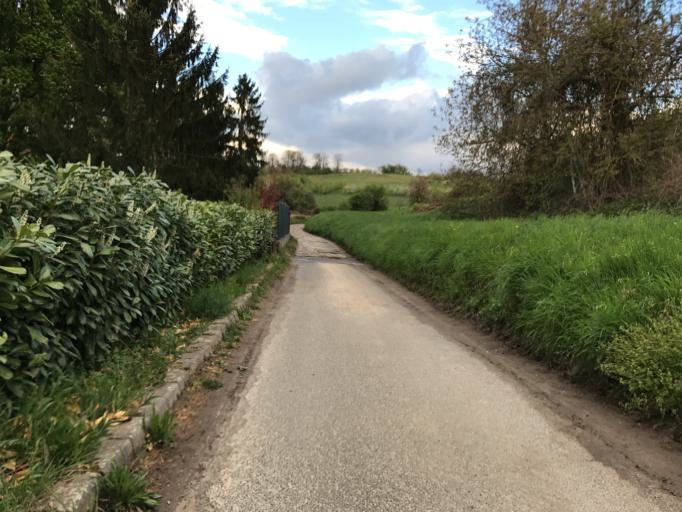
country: DE
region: Rheinland-Pfalz
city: Wackernheim
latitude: 49.9910
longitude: 8.1349
